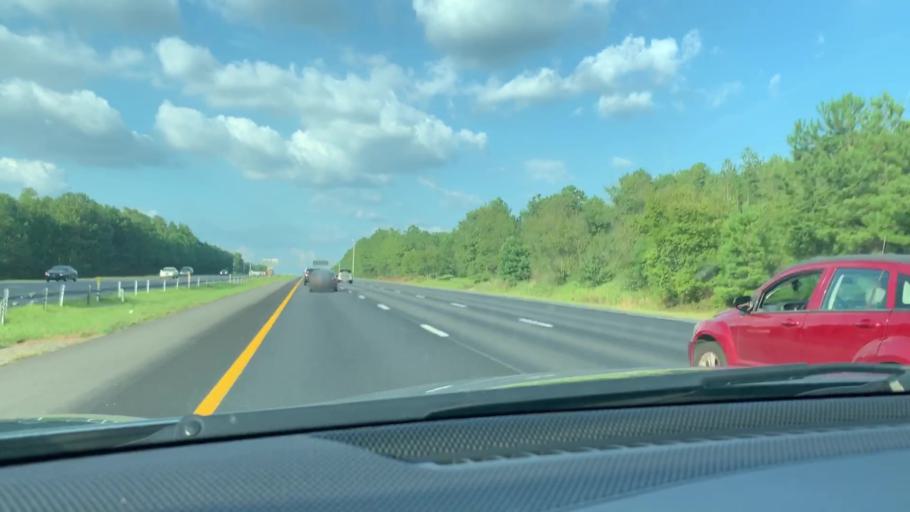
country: US
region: South Carolina
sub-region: Richland County
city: Woodfield
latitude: 34.0261
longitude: -80.9434
